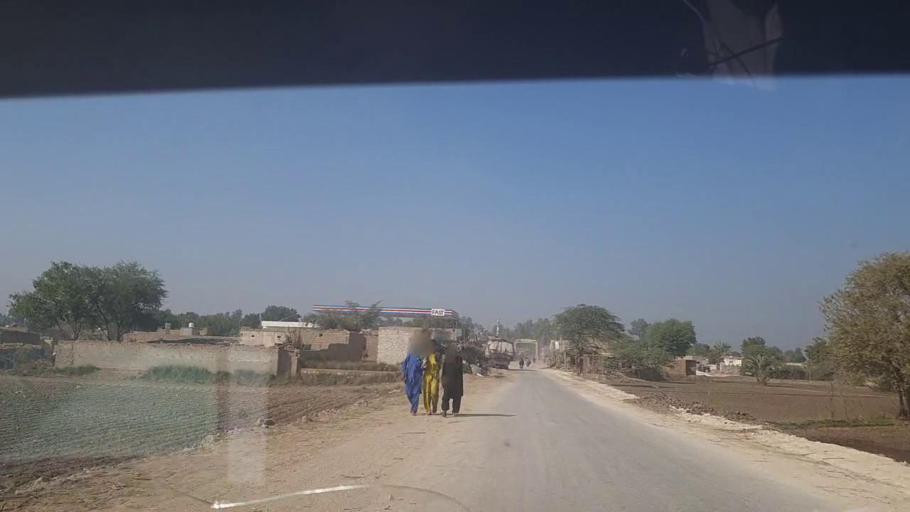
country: PK
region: Sindh
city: Kot Diji
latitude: 27.4296
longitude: 68.6535
